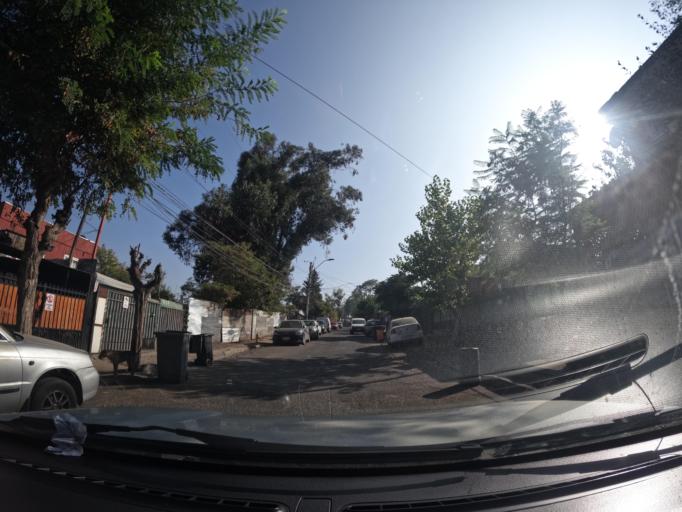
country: CL
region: Santiago Metropolitan
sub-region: Provincia de Santiago
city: Villa Presidente Frei, Nunoa, Santiago, Chile
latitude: -33.4783
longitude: -70.5269
